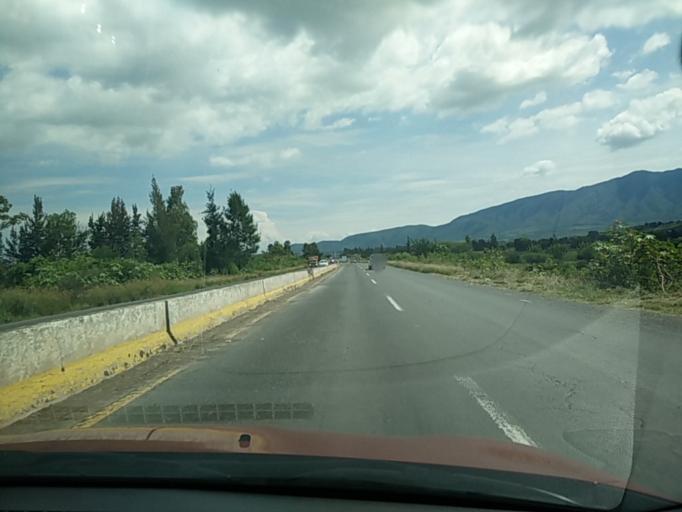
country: MX
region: Jalisco
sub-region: Ixtlahuacan de los Membrillos
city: Los Cedros
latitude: 20.4116
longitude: -103.2323
